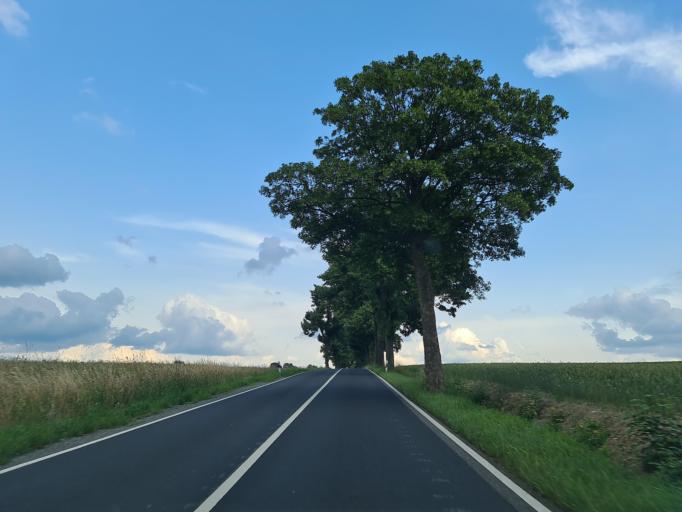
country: DE
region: Saxony
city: Neustadt Vogtland
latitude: 50.4551
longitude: 12.3172
